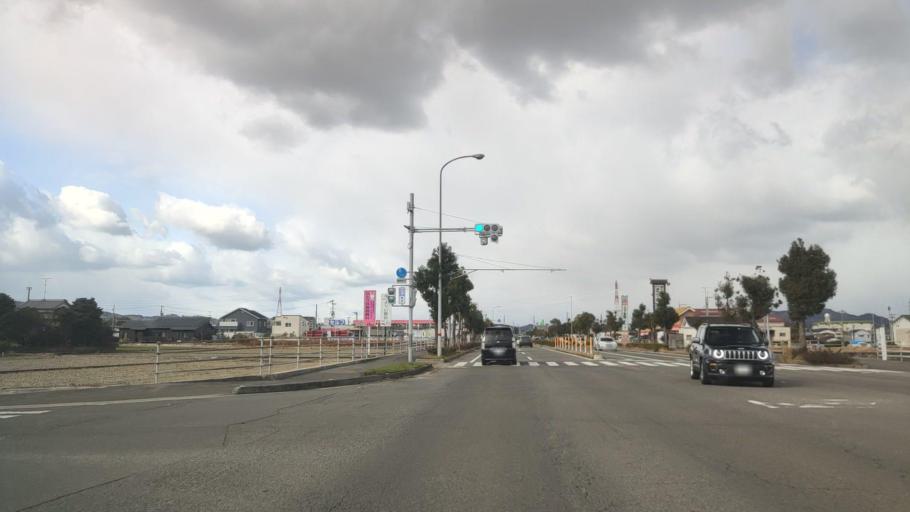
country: JP
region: Ehime
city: Hojo
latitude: 34.0398
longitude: 132.9935
